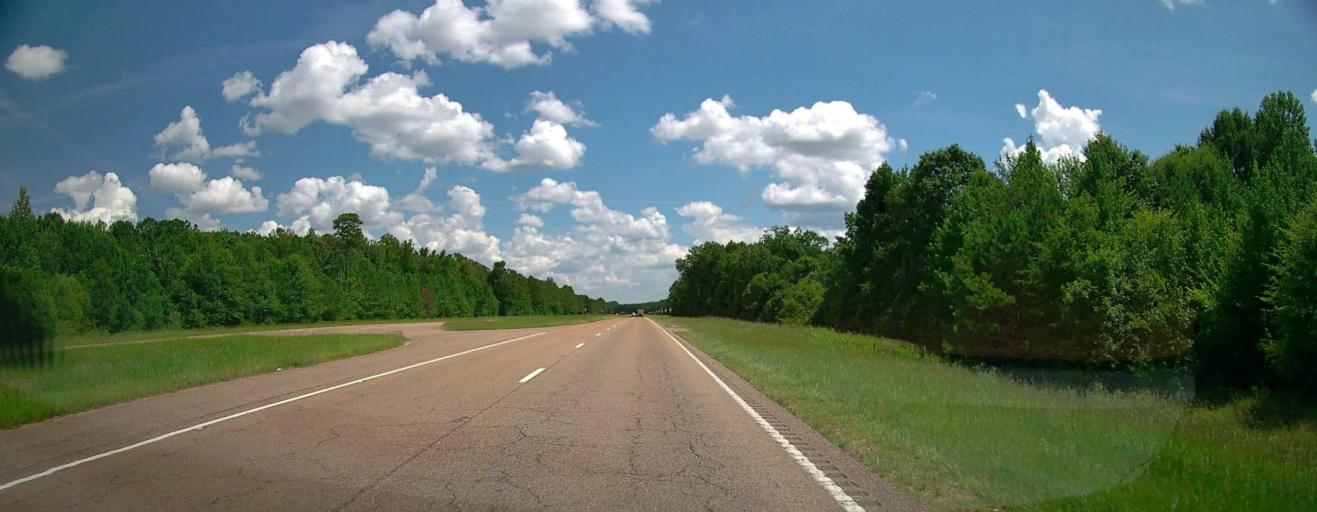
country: US
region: Mississippi
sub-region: Monroe County
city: Aberdeen
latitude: 33.8313
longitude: -88.5877
